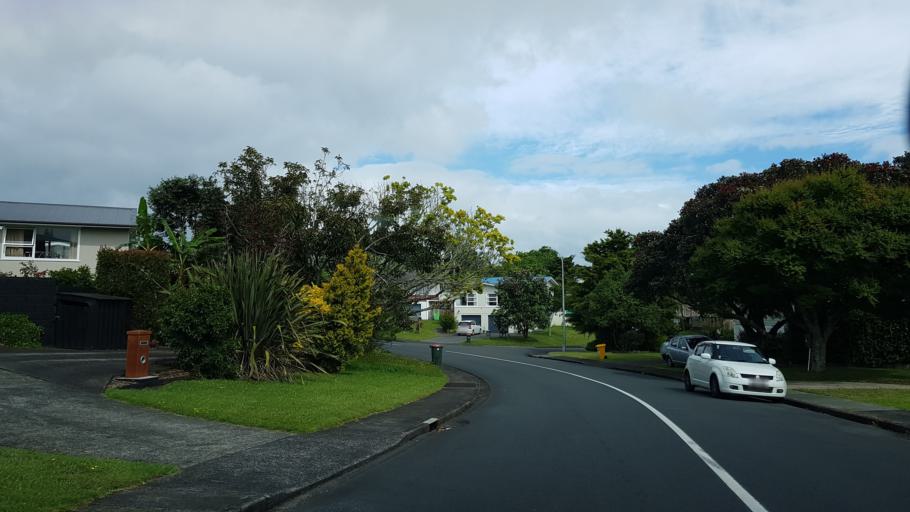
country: NZ
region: Auckland
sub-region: Auckland
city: North Shore
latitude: -36.7881
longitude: 174.7457
